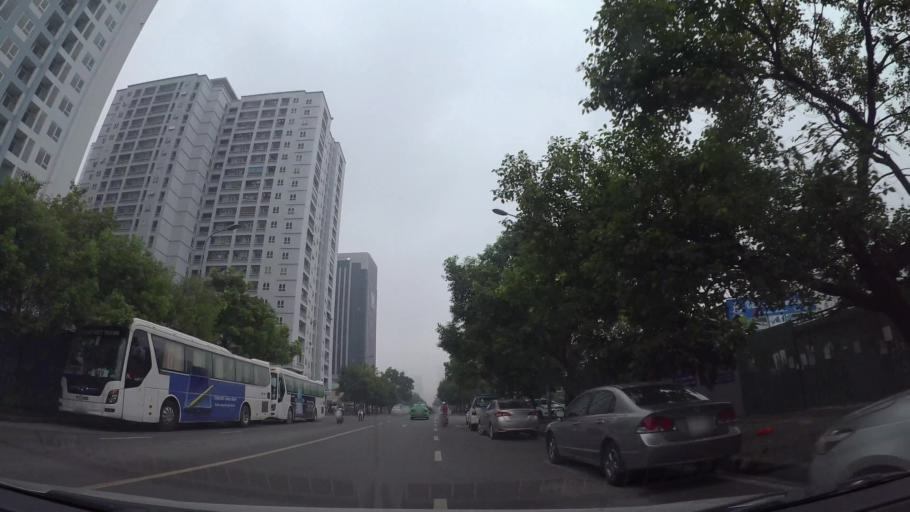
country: VN
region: Ha Noi
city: Cau Giay
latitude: 21.0180
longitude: 105.7874
